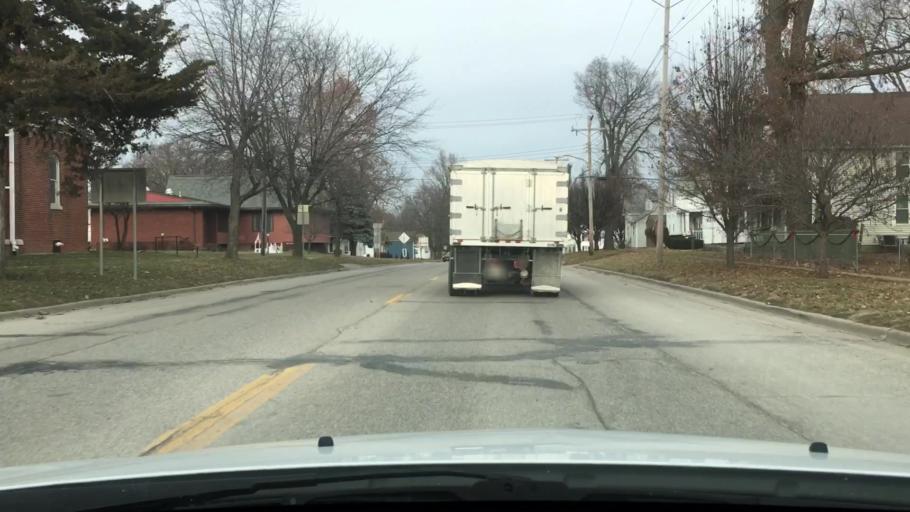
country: US
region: Illinois
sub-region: Pike County
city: Pittsfield
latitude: 39.6080
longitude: -90.8030
